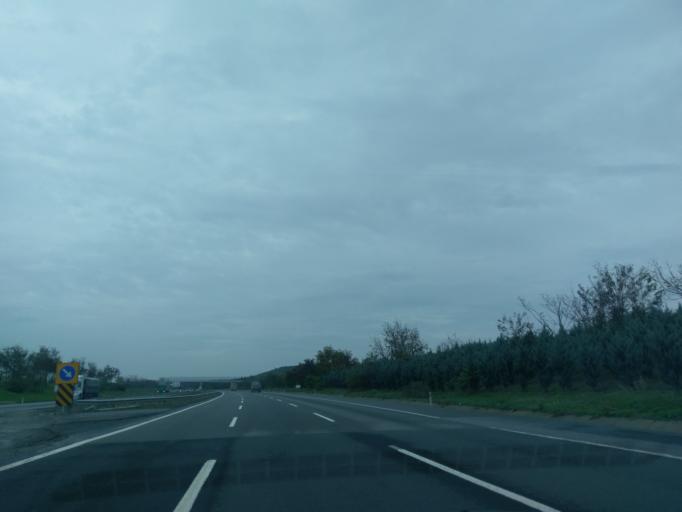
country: TR
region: Istanbul
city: Canta
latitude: 41.1581
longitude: 28.1398
